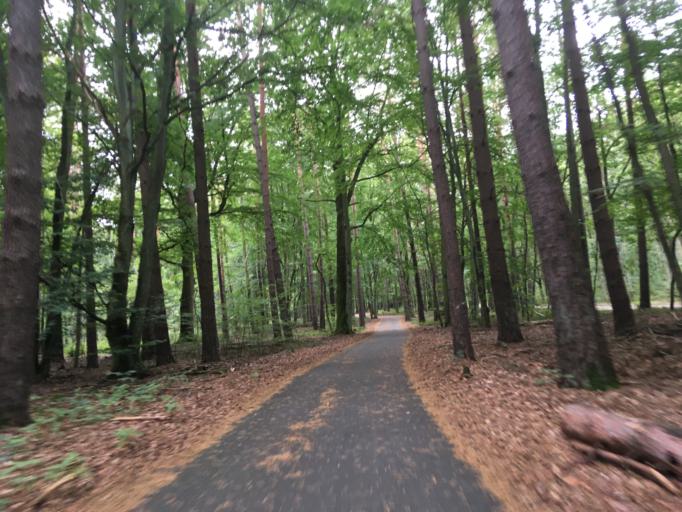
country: DE
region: Brandenburg
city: Friedrichswalde
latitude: 53.0420
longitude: 13.6683
